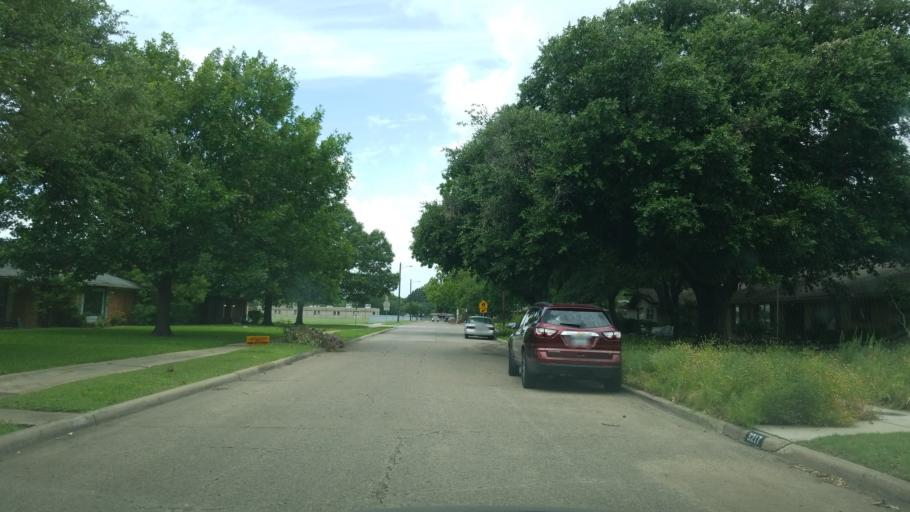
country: US
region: Texas
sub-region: Dallas County
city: Farmers Branch
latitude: 32.8896
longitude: -96.8721
